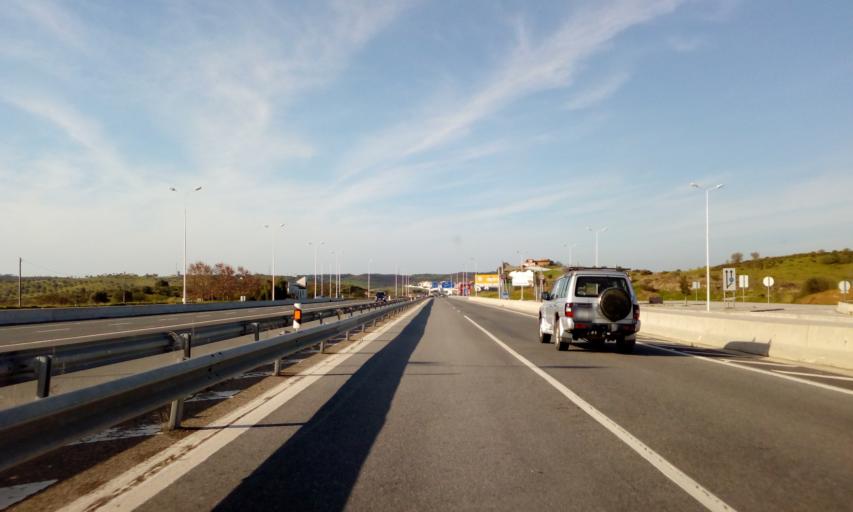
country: PT
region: Faro
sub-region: Castro Marim
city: Castro Marim
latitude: 37.2366
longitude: -7.4371
